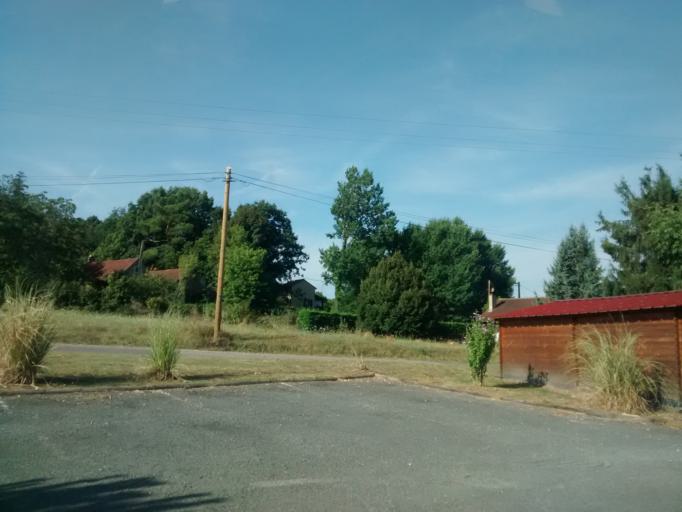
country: FR
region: Aquitaine
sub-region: Departement de la Dordogne
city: Sarlat-la-Caneda
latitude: 44.9288
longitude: 1.2044
